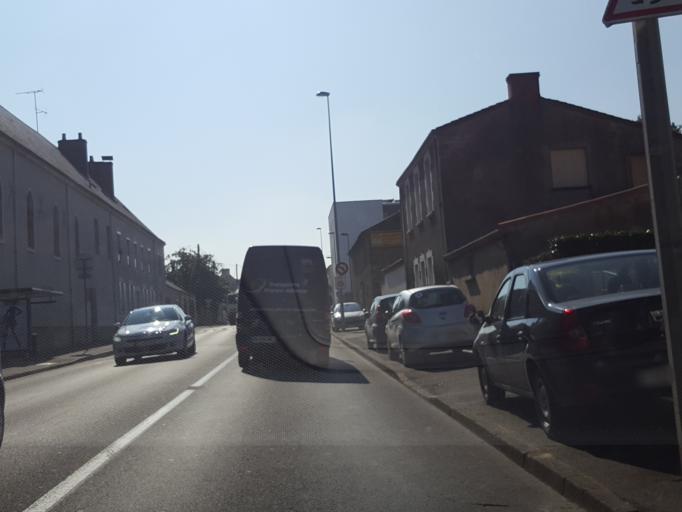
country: FR
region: Pays de la Loire
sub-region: Departement de la Vendee
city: La Roche-sur-Yon
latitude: 46.6619
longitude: -1.4223
